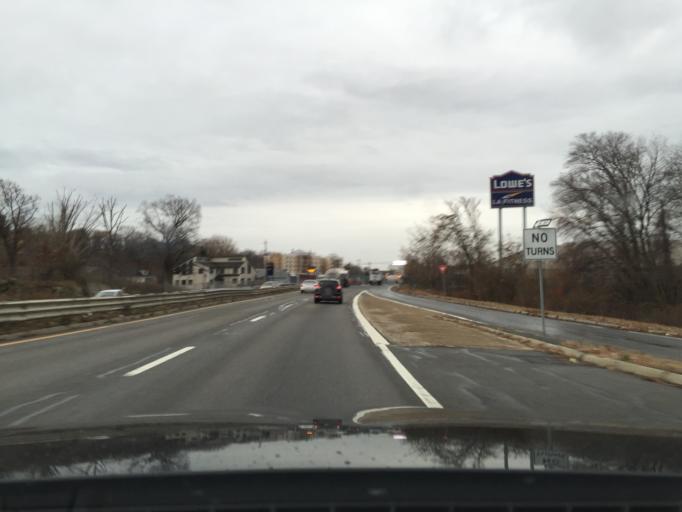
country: US
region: Massachusetts
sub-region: Essex County
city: Saugus
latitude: 42.4495
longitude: -71.0237
